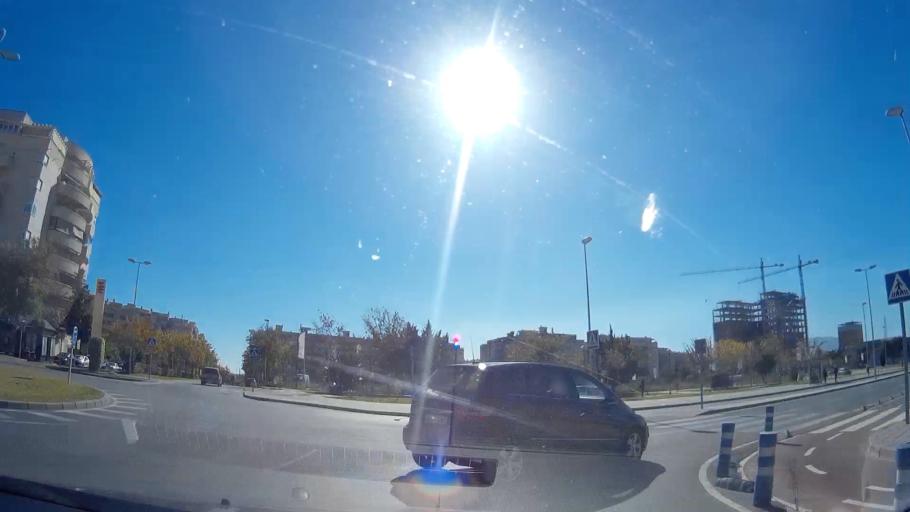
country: ES
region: Andalusia
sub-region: Provincia de Malaga
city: Malaga
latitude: 36.7179
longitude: -4.4643
